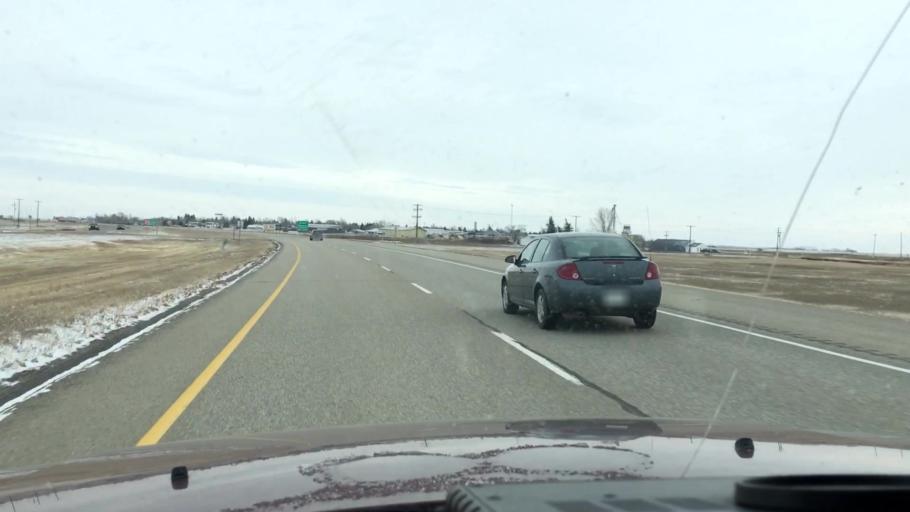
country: CA
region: Saskatchewan
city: Watrous
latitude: 51.2741
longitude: -106.0061
